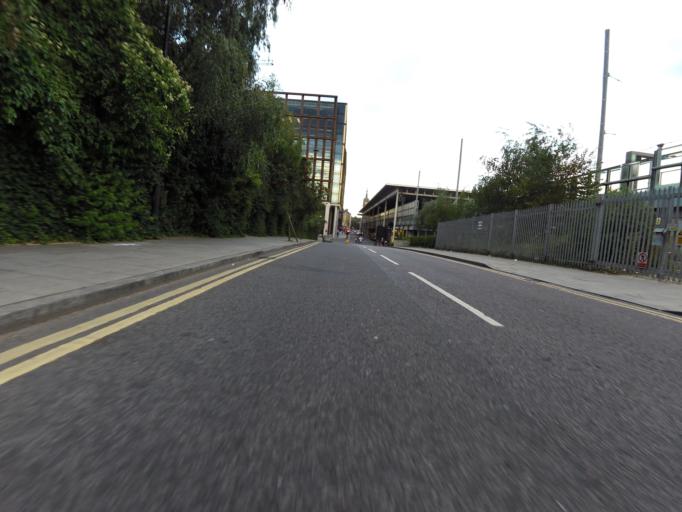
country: GB
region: England
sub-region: Greater London
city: Barnsbury
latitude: 51.5349
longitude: -0.1278
